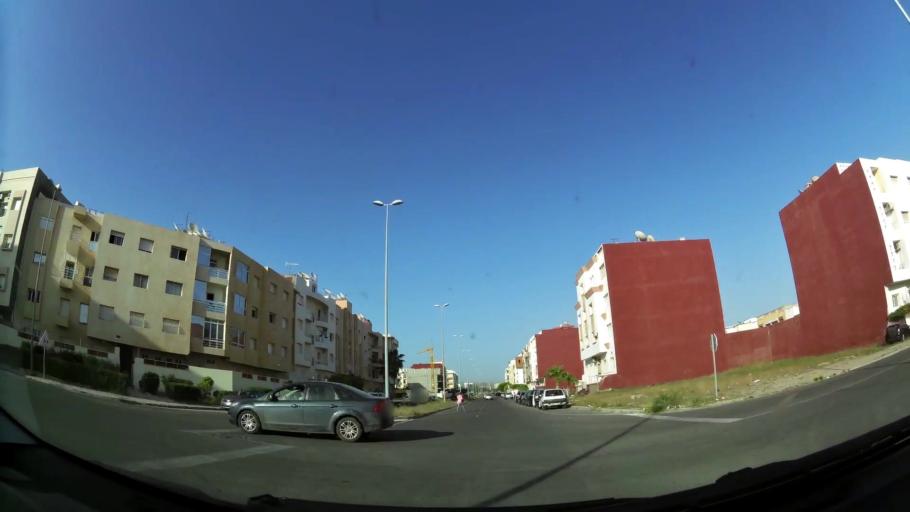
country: MA
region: Oued ed Dahab-Lagouira
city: Dakhla
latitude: 30.4006
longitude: -9.5342
